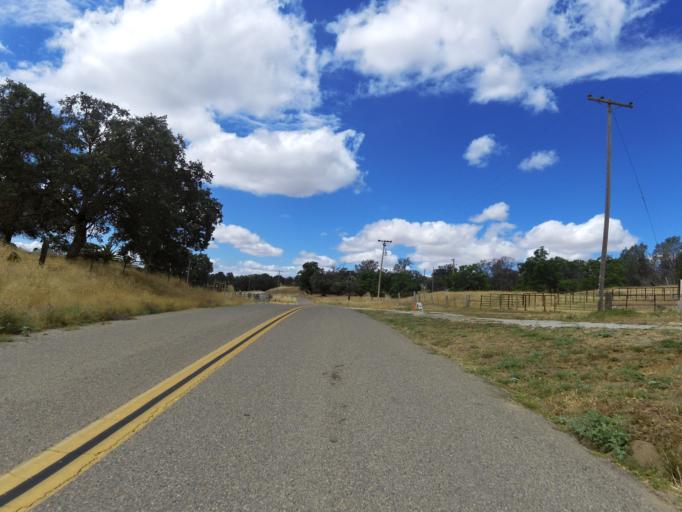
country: US
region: California
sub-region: Madera County
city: Yosemite Lakes
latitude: 37.2166
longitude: -119.8782
